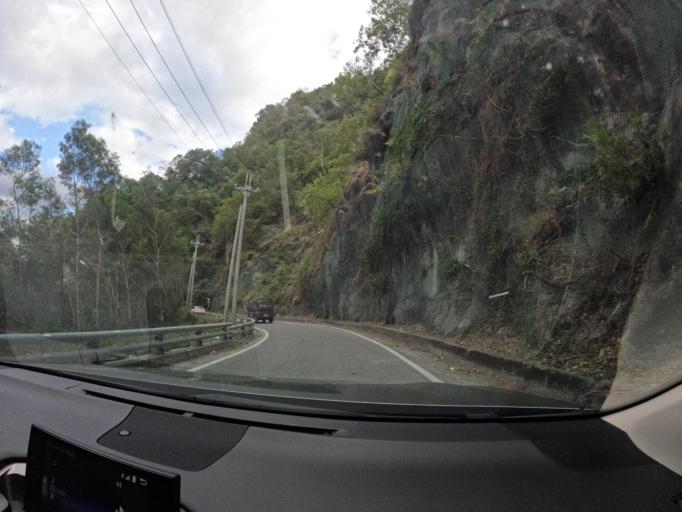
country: TW
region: Taiwan
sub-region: Taitung
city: Taitung
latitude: 23.1353
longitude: 121.1144
